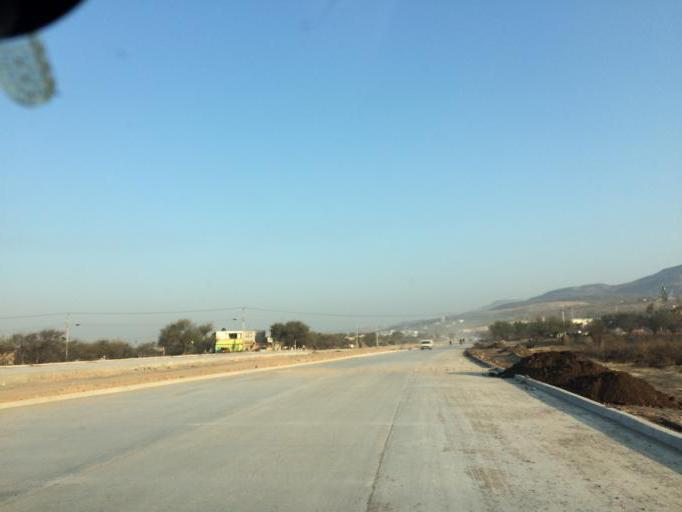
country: MX
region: Guanajuato
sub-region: Leon
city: Fraccionamiento Paraiso Real
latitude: 21.1153
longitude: -101.5898
